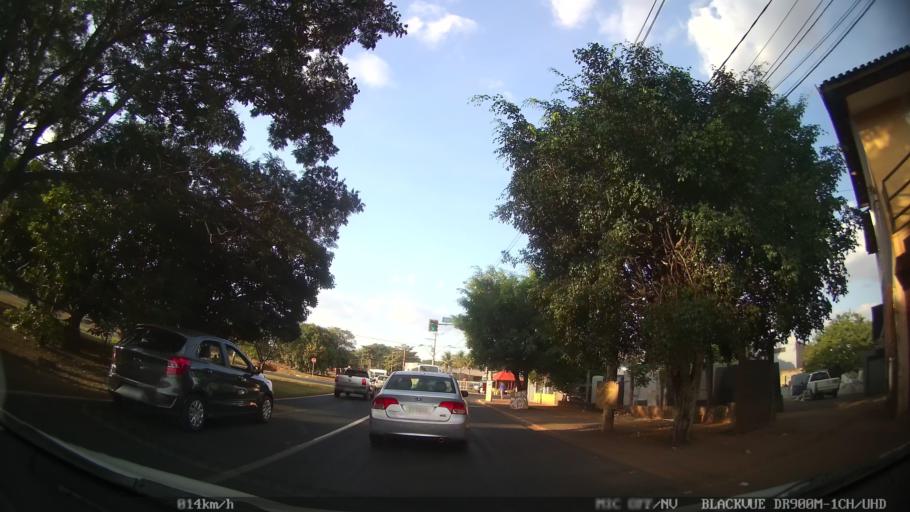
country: BR
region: Sao Paulo
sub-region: Ribeirao Preto
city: Ribeirao Preto
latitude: -21.1288
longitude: -47.7869
